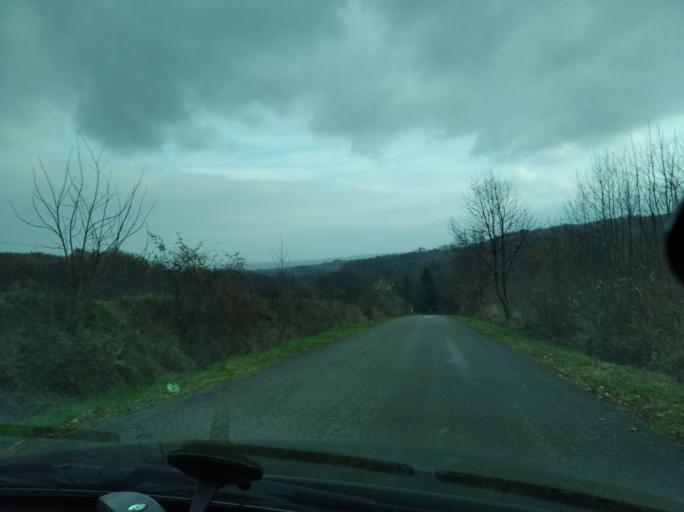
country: PL
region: Subcarpathian Voivodeship
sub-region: Powiat przeworski
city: Sietesz
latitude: 49.9681
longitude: 22.3416
